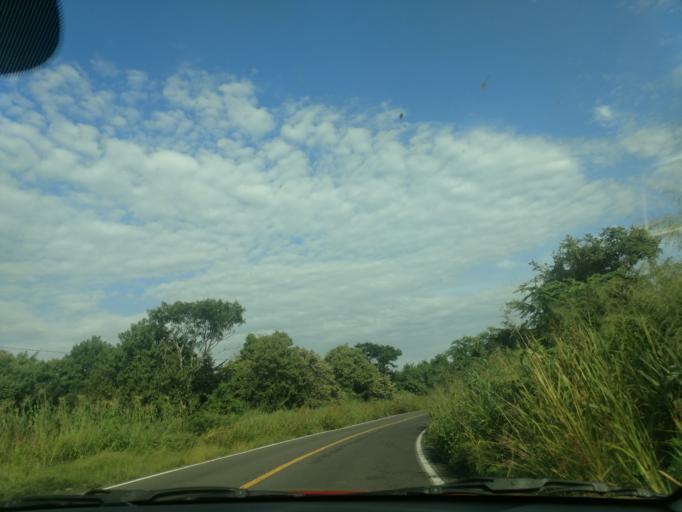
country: MX
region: Jalisco
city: Ameca
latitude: 20.5201
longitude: -104.1197
